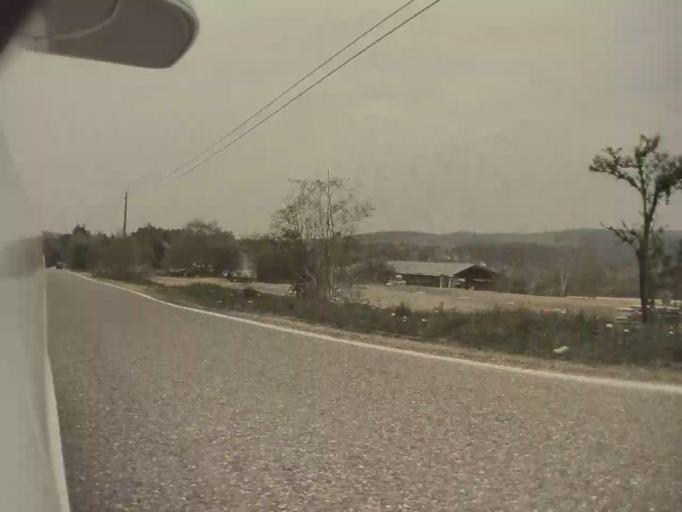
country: BE
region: Wallonia
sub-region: Province du Luxembourg
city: La Roche-en-Ardenne
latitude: 50.2282
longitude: 5.6242
